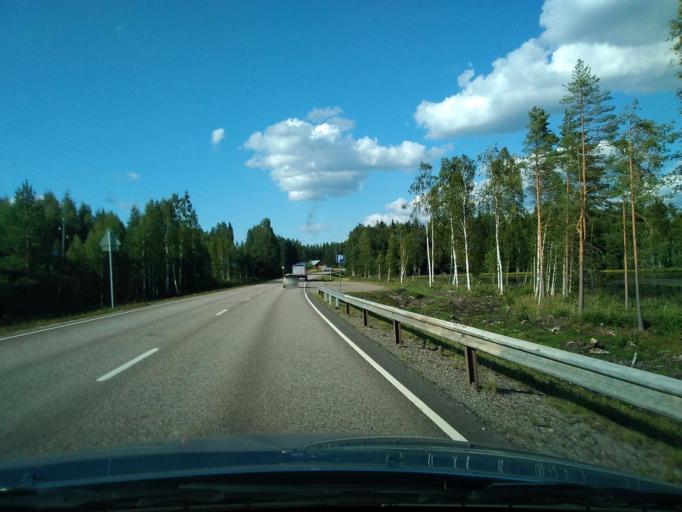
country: FI
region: Pirkanmaa
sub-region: Ylae-Pirkanmaa
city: Maenttae
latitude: 62.0935
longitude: 24.7278
